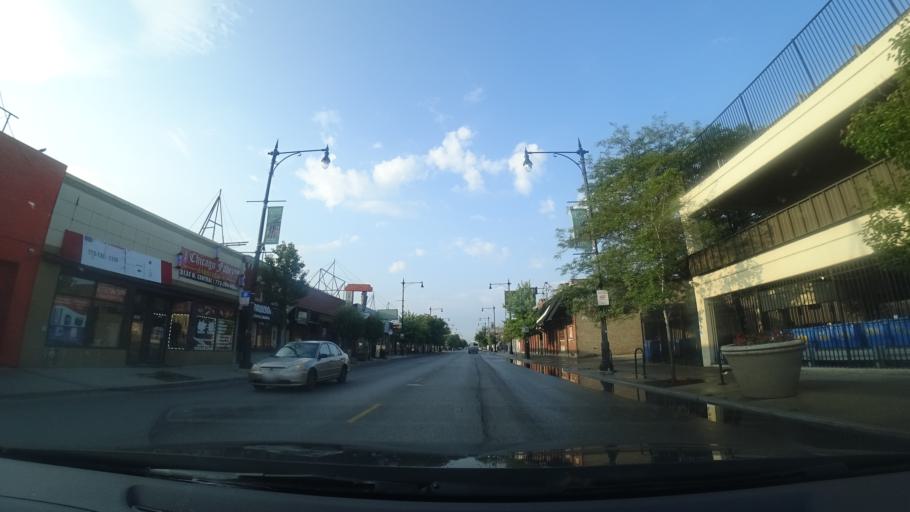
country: US
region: Illinois
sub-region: Cook County
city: Elmwood Park
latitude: 41.9380
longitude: -87.7665
